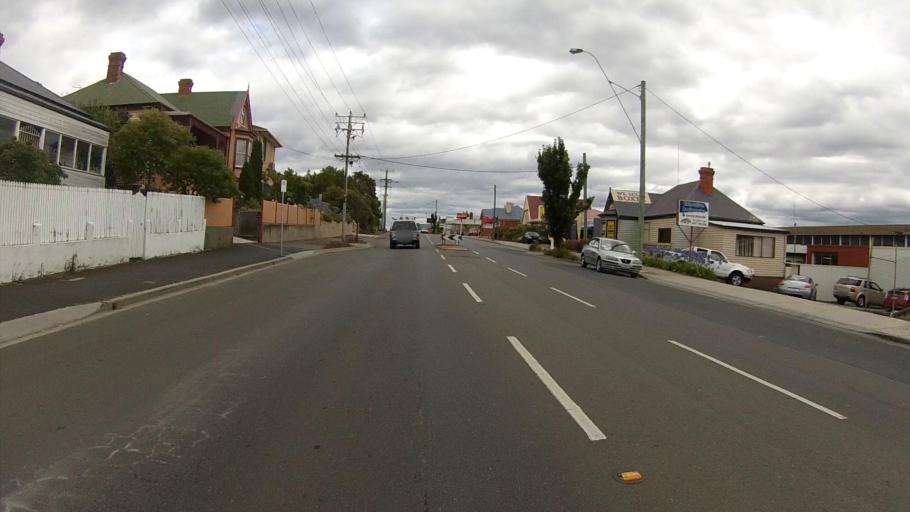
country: AU
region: Tasmania
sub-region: Glenorchy
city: Glenorchy
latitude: -42.8287
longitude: 147.2683
